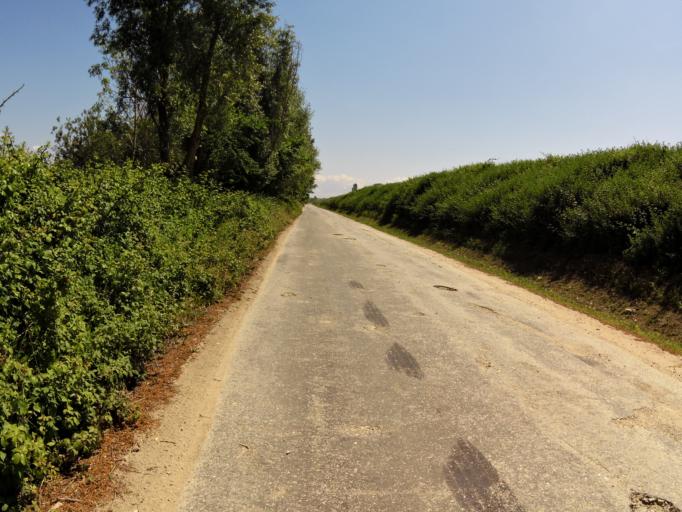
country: PT
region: Coimbra
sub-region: Montemor-O-Velho
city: Montemor-o-Velho
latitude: 40.1487
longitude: -8.7308
